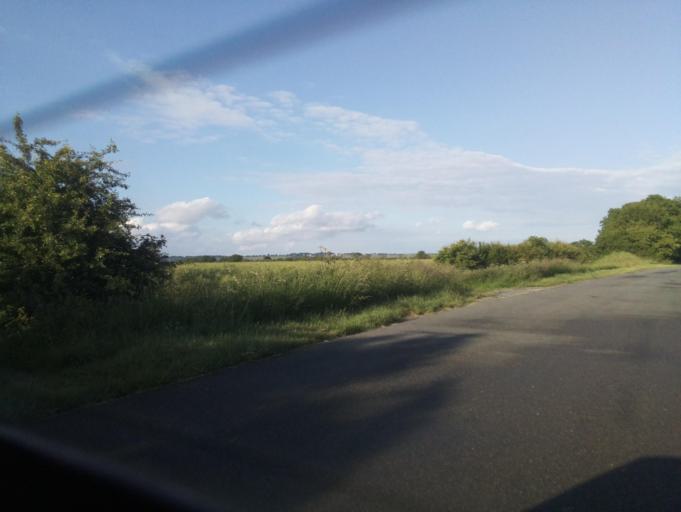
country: GB
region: England
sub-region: Lincolnshire
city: Navenby
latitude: 53.1135
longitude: -0.6022
